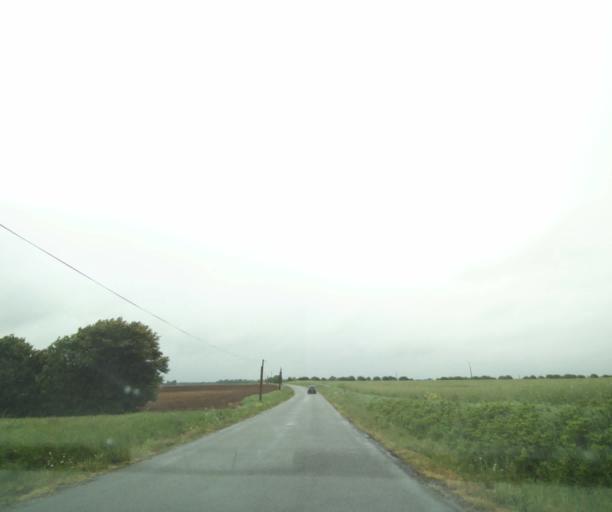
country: FR
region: Poitou-Charentes
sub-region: Departement de la Charente-Maritime
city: Corme-Royal
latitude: 45.7095
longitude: -0.7969
